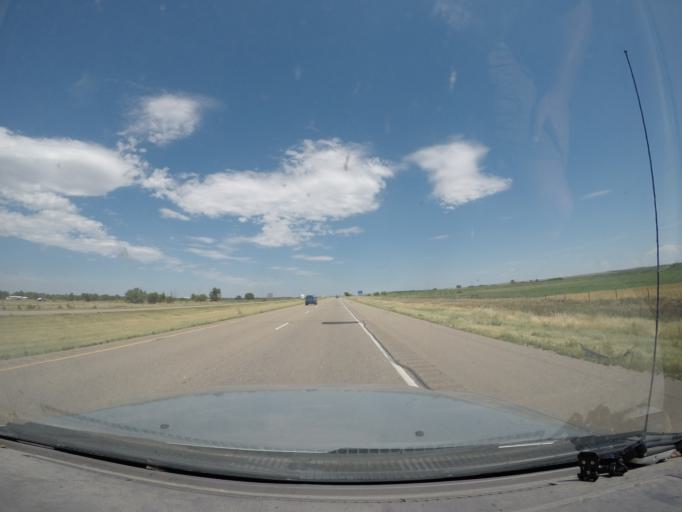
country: US
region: Colorado
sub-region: Sedgwick County
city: Julesburg
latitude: 41.0397
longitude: -102.1116
